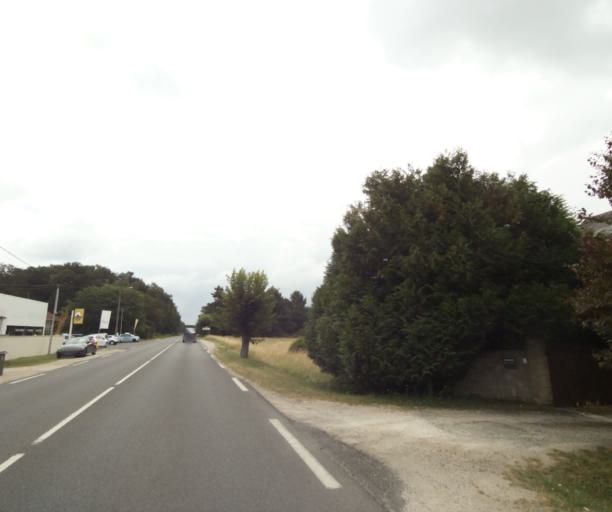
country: FR
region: Centre
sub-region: Departement du Loiret
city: Mardie
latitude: 47.8880
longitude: 2.0646
